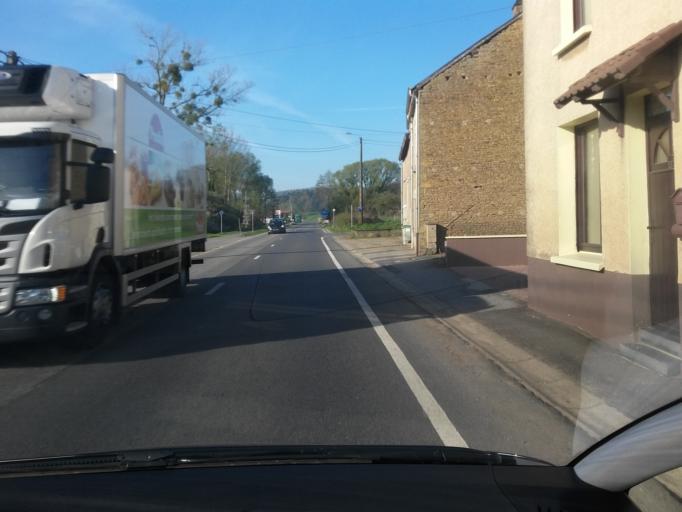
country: BE
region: Wallonia
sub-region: Province du Luxembourg
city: Rouvroy
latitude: 49.5509
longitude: 5.4968
